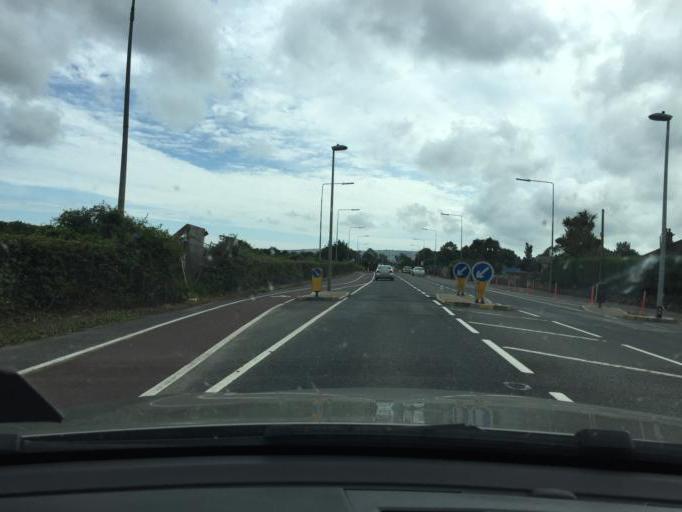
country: IE
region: Munster
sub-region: Waterford
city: Dungarvan
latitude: 52.1014
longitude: -7.6063
